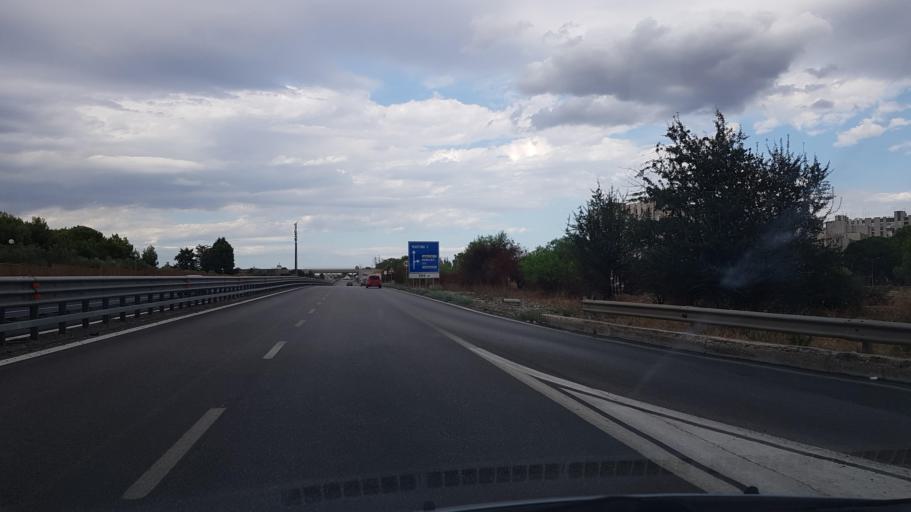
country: IT
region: Apulia
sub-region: Provincia di Taranto
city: Paolo VI
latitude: 40.5183
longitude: 17.2576
